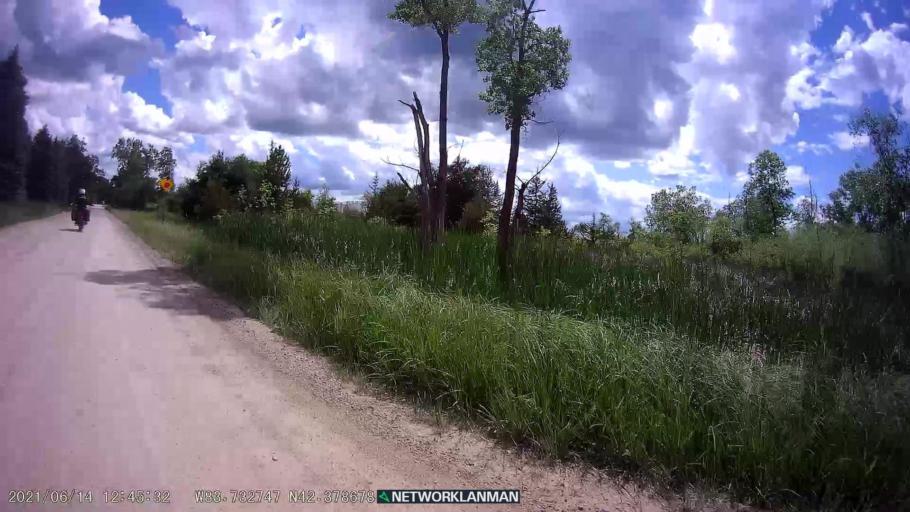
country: US
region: Michigan
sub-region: Livingston County
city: Whitmore Lake
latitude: 42.3785
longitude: -83.7326
